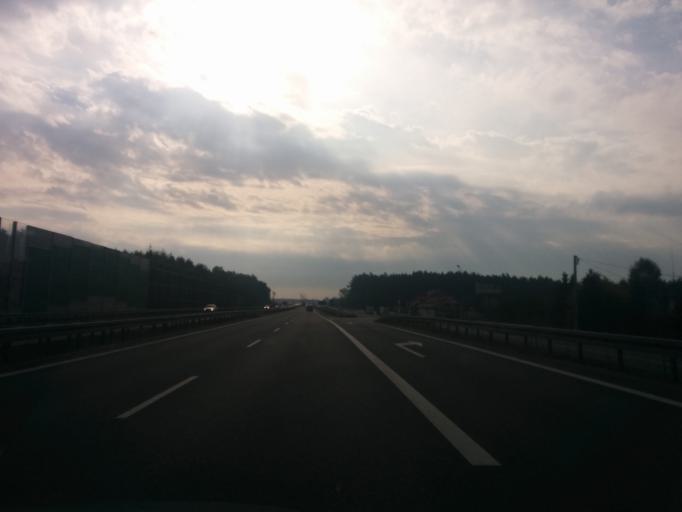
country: PL
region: Masovian Voivodeship
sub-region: Powiat bialobrzeski
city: Stara Blotnica
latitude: 51.5784
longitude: 21.0050
